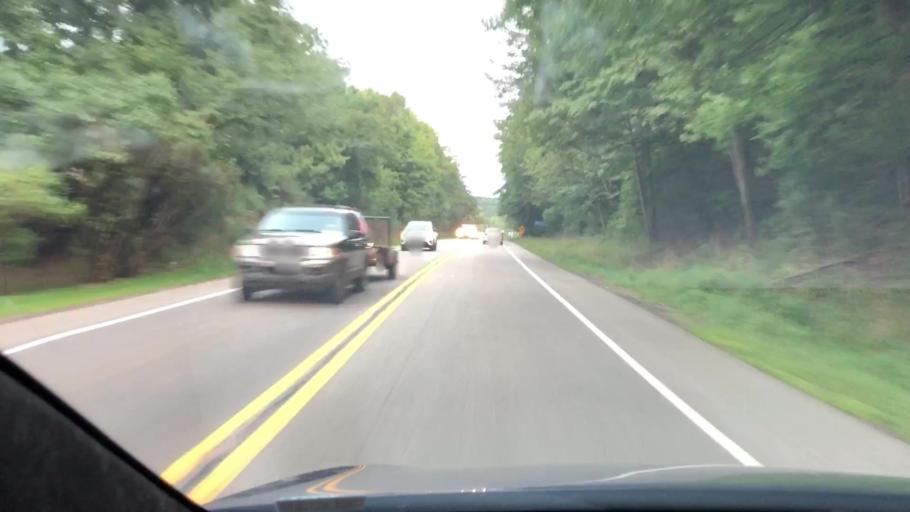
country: US
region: Pennsylvania
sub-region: Butler County
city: Slippery Rock
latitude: 40.9969
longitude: -79.9877
